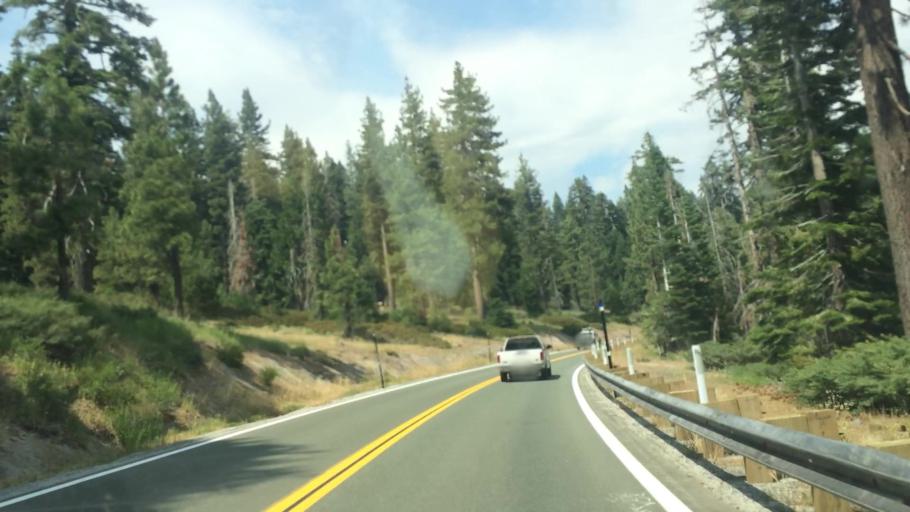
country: US
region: California
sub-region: Calaveras County
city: Arnold
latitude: 38.5767
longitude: -120.2607
